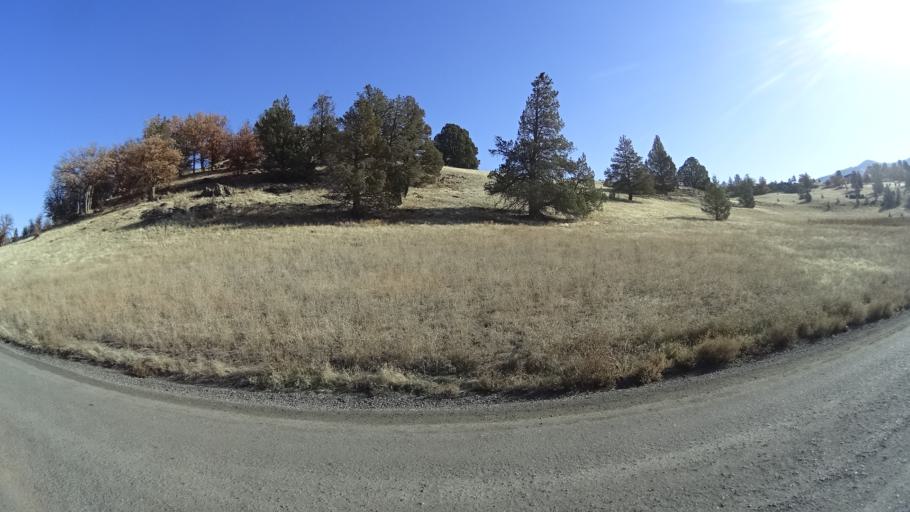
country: US
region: California
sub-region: Siskiyou County
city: Montague
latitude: 41.8855
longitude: -122.4266
